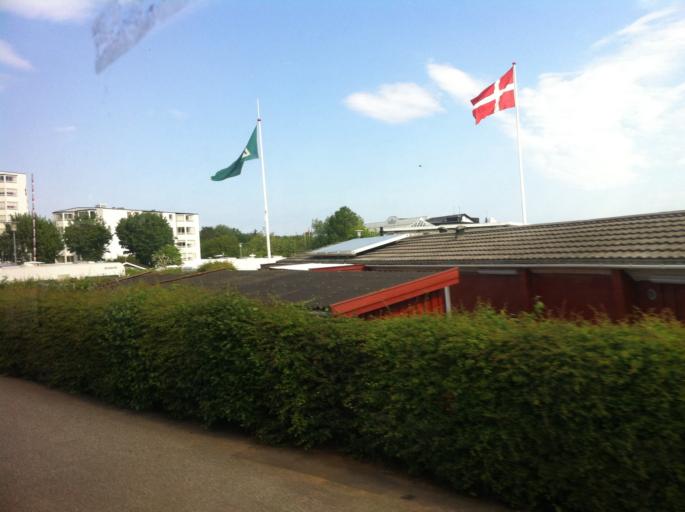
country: DK
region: Capital Region
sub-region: Helsingor Kommune
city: Helsingor
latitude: 56.0431
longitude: 12.6053
